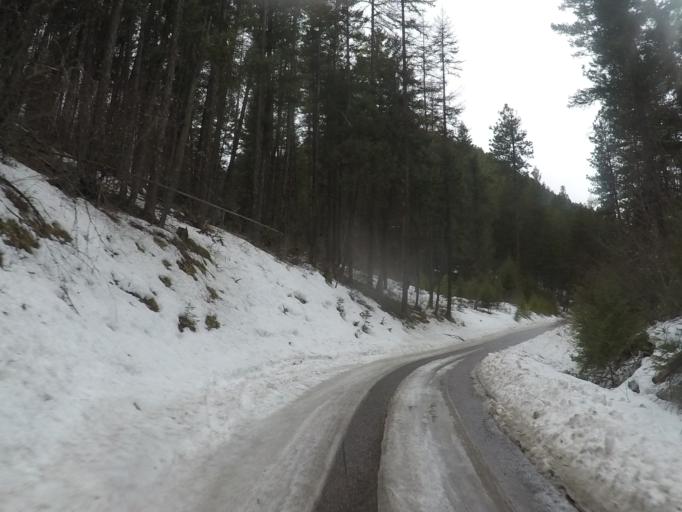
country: US
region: Montana
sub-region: Missoula County
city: East Missoula
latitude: 46.9251
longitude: -113.9635
